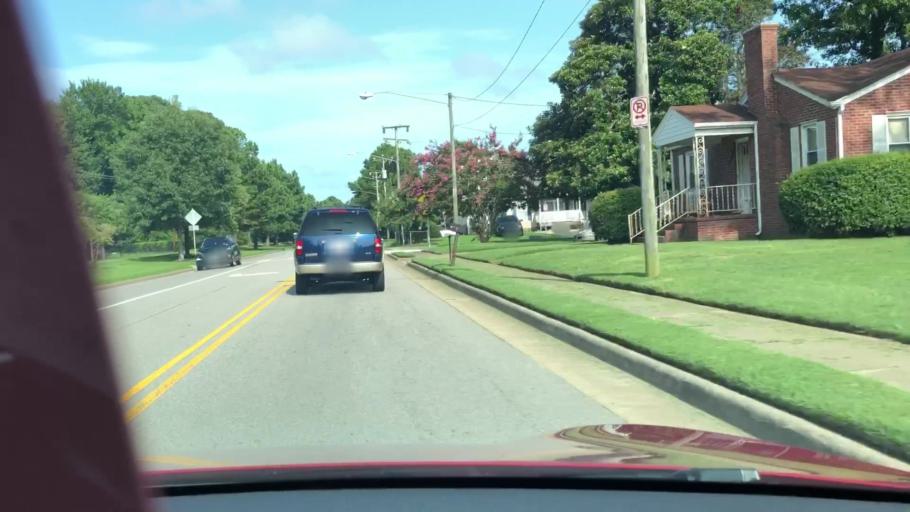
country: US
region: Virginia
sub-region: City of Virginia Beach
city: Virginia Beach
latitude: 36.8379
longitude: -75.9957
